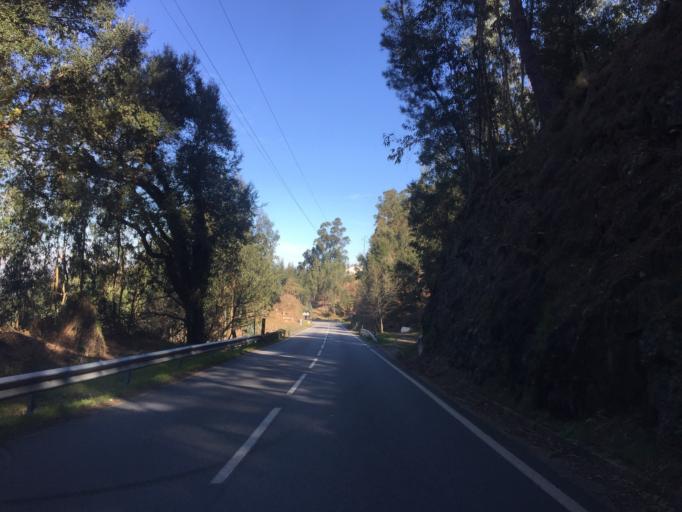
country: PT
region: Aveiro
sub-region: Vale de Cambra
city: Macieira de Cambra
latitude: 40.9035
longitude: -8.3284
